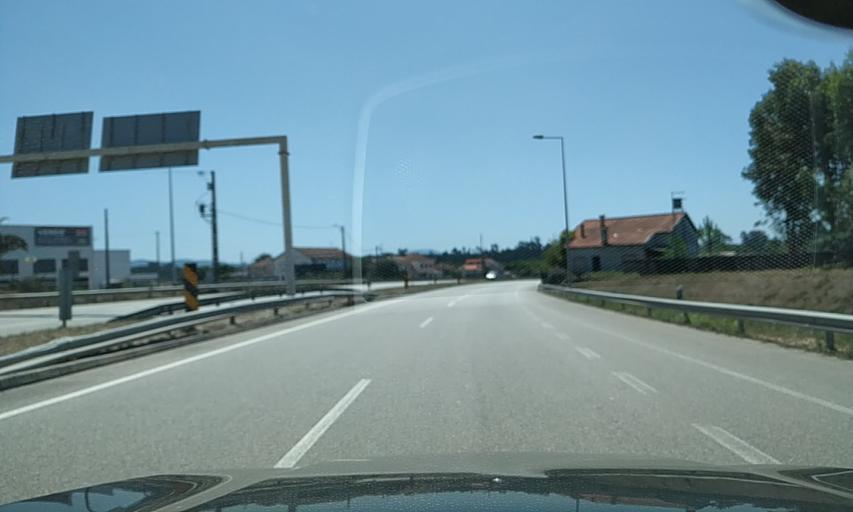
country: PT
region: Aveiro
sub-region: Agueda
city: Aguada de Cima
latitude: 40.5205
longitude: -8.4494
